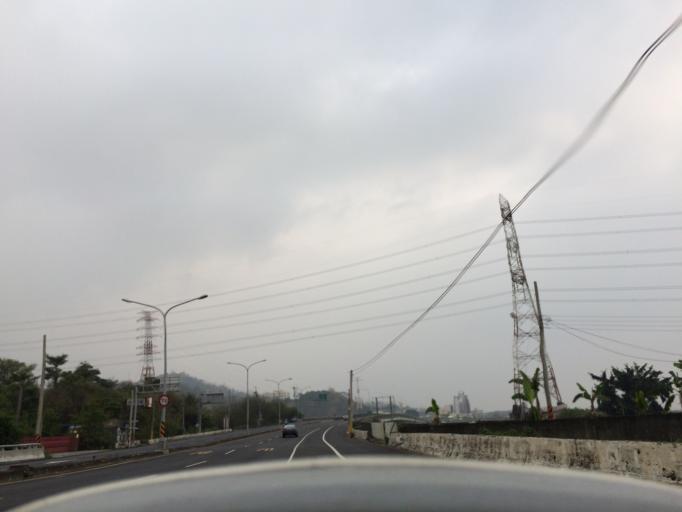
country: TW
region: Taiwan
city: Zhongxing New Village
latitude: 24.0127
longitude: 120.6957
